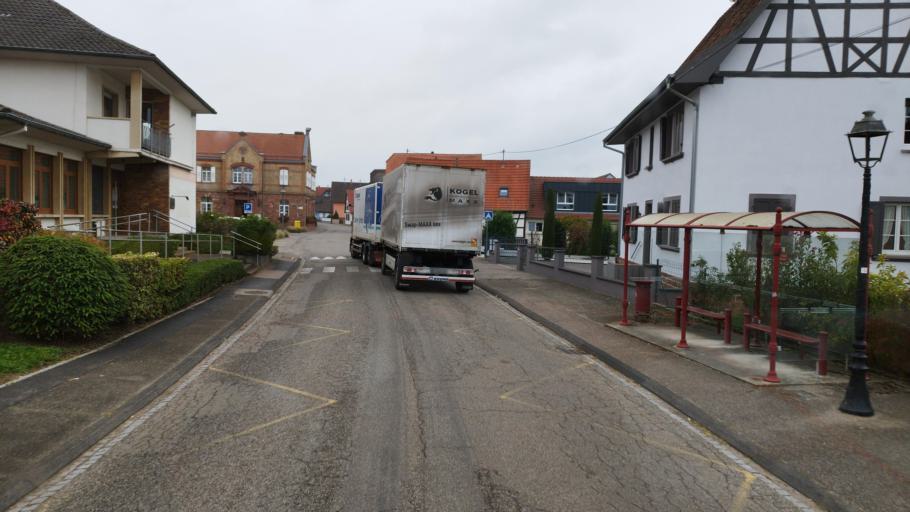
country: DE
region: Rheinland-Pfalz
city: Kapsweyer
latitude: 48.9886
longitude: 8.0460
